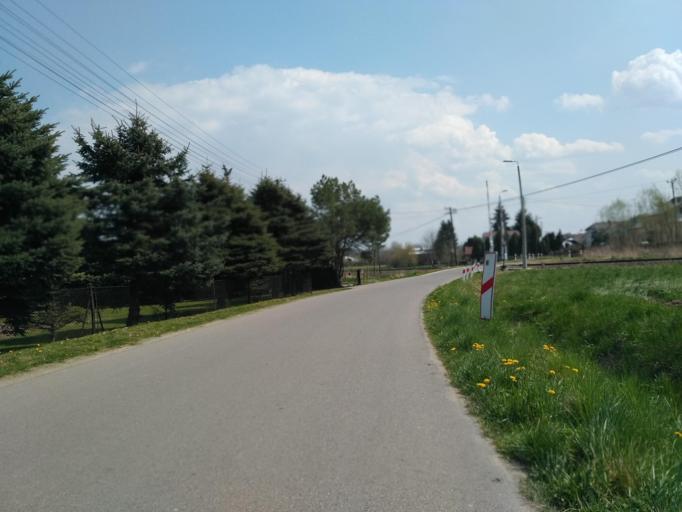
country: PL
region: Subcarpathian Voivodeship
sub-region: Powiat jasielski
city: Tarnowiec
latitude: 49.7346
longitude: 21.6070
